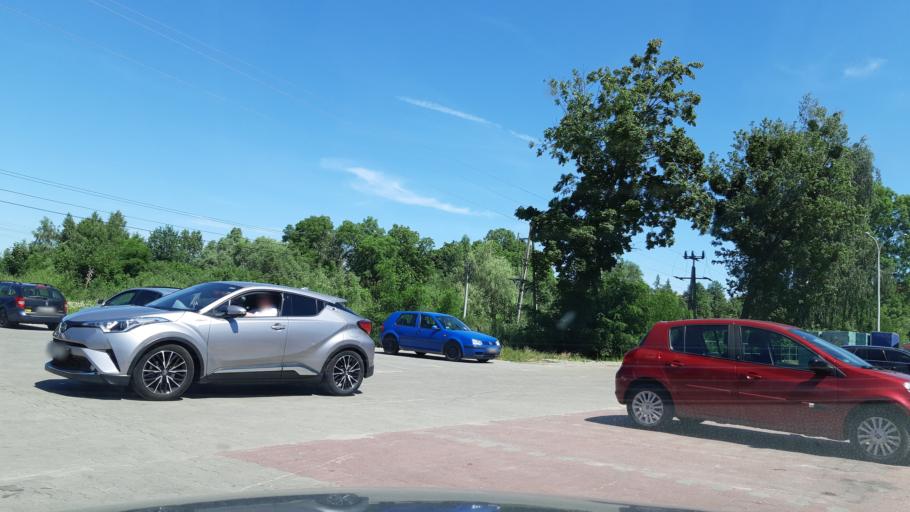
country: PL
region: Warmian-Masurian Voivodeship
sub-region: Powiat mragowski
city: Mikolajki
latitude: 53.8048
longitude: 21.5720
